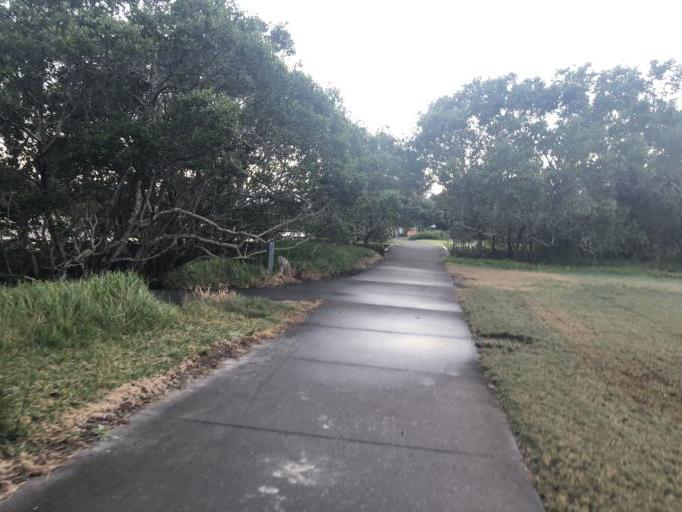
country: AU
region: New South Wales
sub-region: Coffs Harbour
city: Coffs Harbour
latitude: -30.2990
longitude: 153.1348
